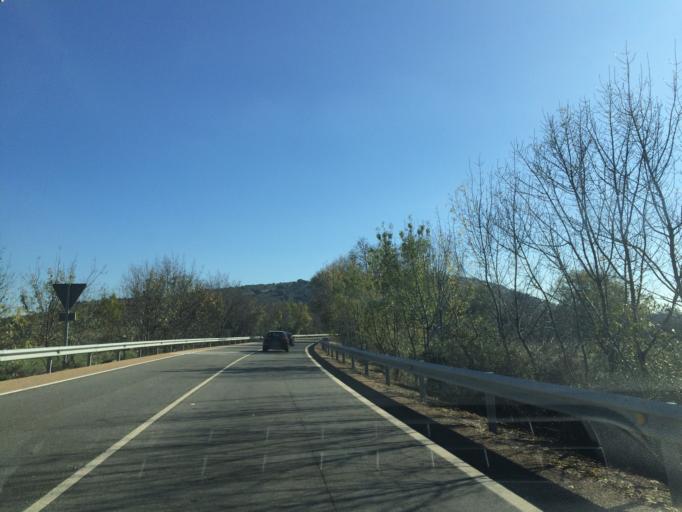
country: ES
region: Madrid
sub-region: Provincia de Madrid
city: Guadalix de la Sierra
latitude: 40.7934
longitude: -3.6907
